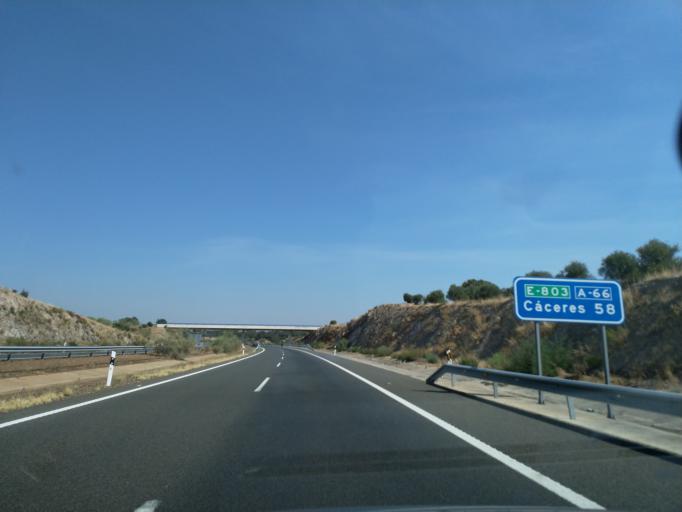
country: ES
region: Extremadura
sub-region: Provincia de Badajoz
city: Mirandilla
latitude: 38.9872
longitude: -6.3308
